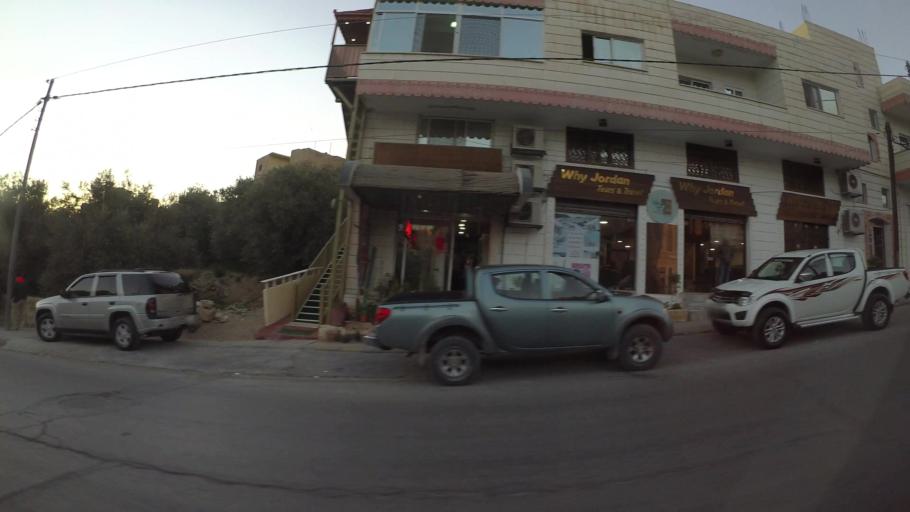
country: JO
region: Ma'an
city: Petra
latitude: 30.3257
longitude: 35.4737
